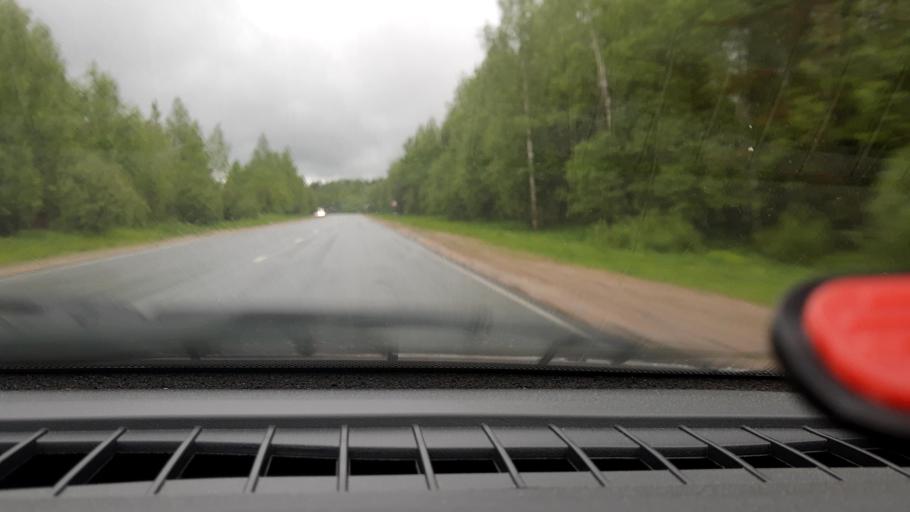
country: RU
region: Nizjnij Novgorod
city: Semenov
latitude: 56.7891
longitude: 44.4497
